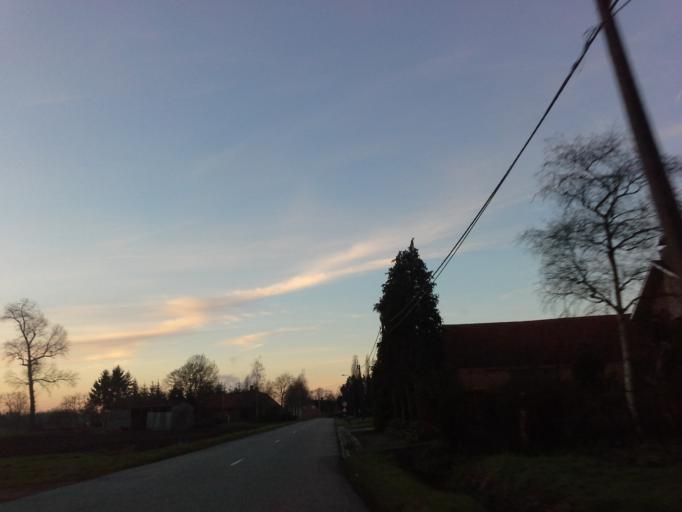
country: BE
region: Flanders
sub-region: Provincie Antwerpen
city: Meerhout
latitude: 51.1183
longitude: 5.0653
